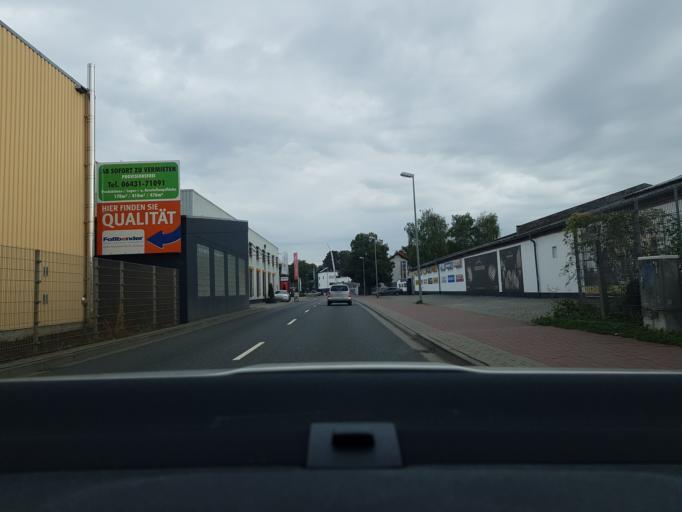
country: DE
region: Hesse
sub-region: Regierungsbezirk Giessen
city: Limburg an der Lahn
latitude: 50.3795
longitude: 8.0566
